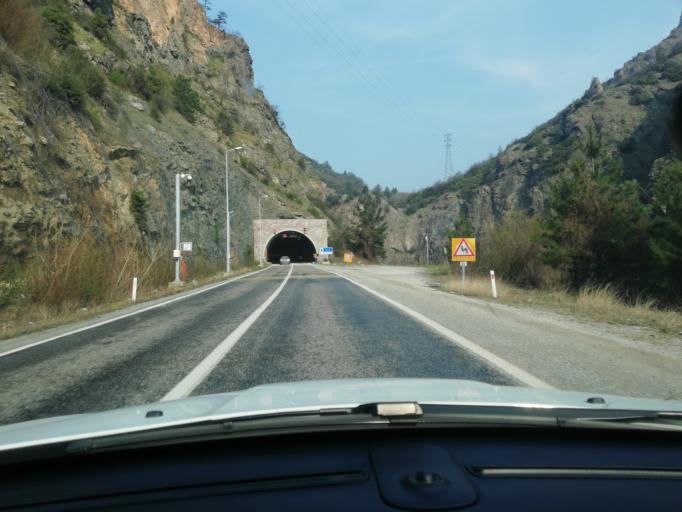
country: TR
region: Karabuk
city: Karabuk
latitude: 41.1526
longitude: 32.5282
